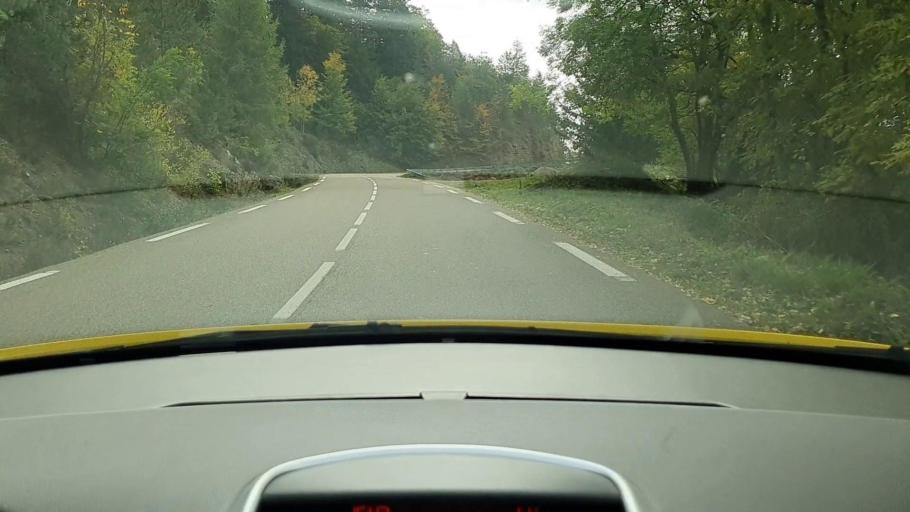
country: FR
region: Languedoc-Roussillon
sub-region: Departement de la Lozere
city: Meyrueis
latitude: 44.1248
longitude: 3.4478
